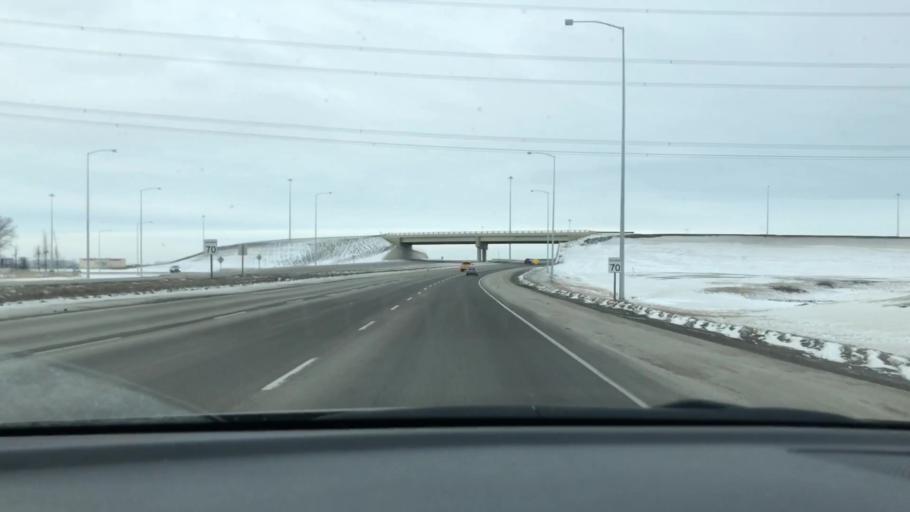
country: CA
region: Alberta
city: Sherwood Park
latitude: 53.5123
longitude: -113.3363
